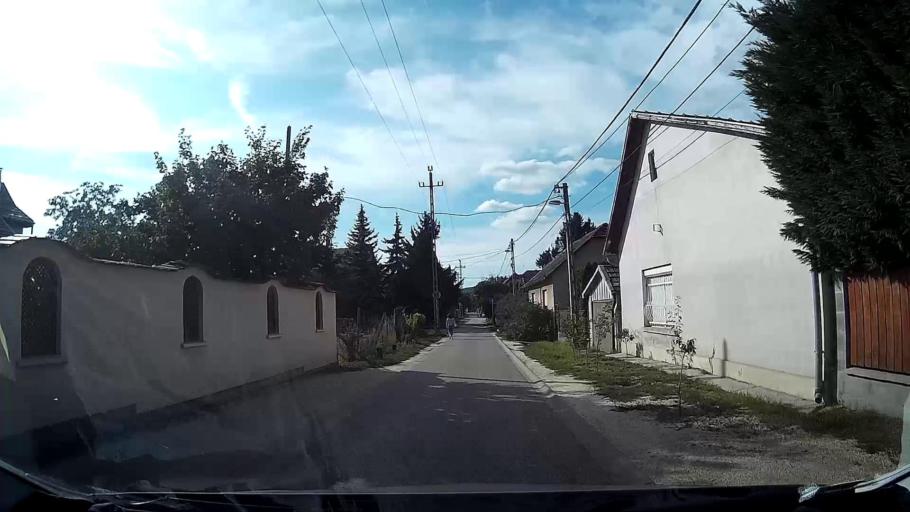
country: HU
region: Pest
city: Pomaz
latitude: 47.6427
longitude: 19.0280
